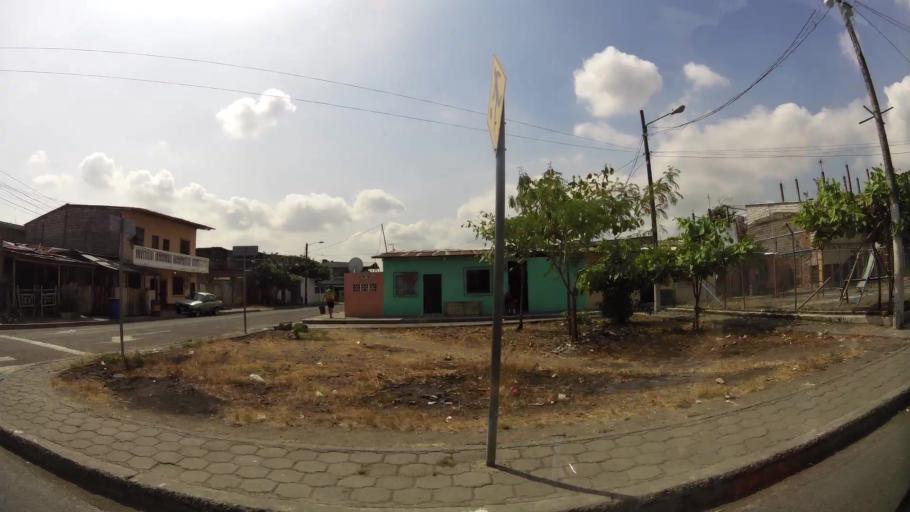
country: EC
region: Guayas
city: Eloy Alfaro
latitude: -2.1525
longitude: -79.8283
